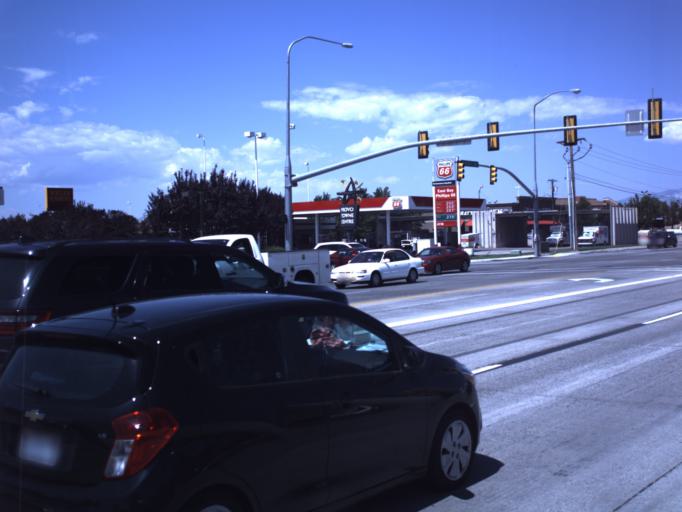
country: US
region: Utah
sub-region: Utah County
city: Provo
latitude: 40.2172
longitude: -111.6589
